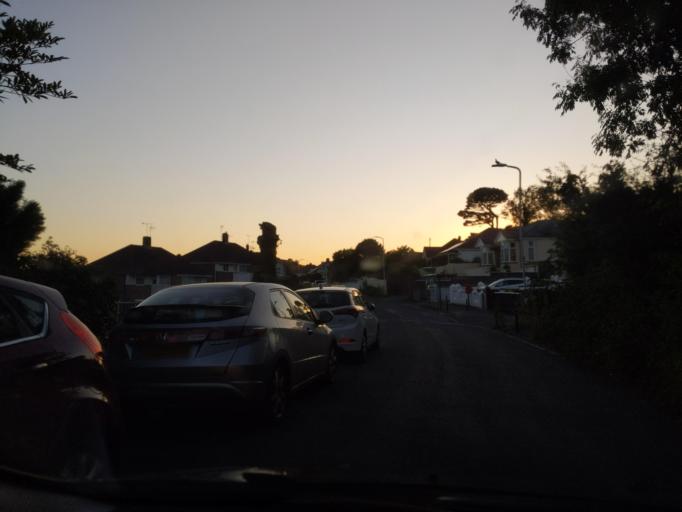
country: GB
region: England
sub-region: Cornwall
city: Torpoint
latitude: 50.4034
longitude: -4.1968
